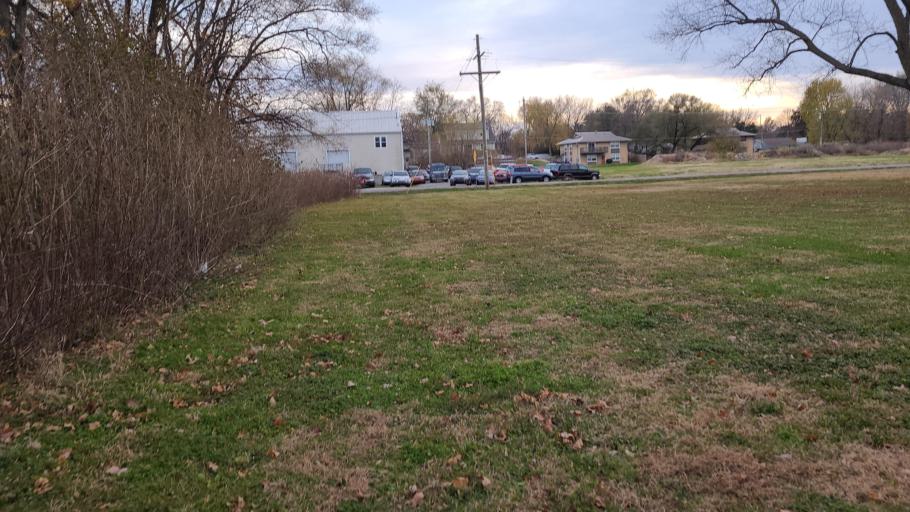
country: US
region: Kansas
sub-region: Douglas County
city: Lawrence
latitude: 38.9811
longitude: -95.2216
